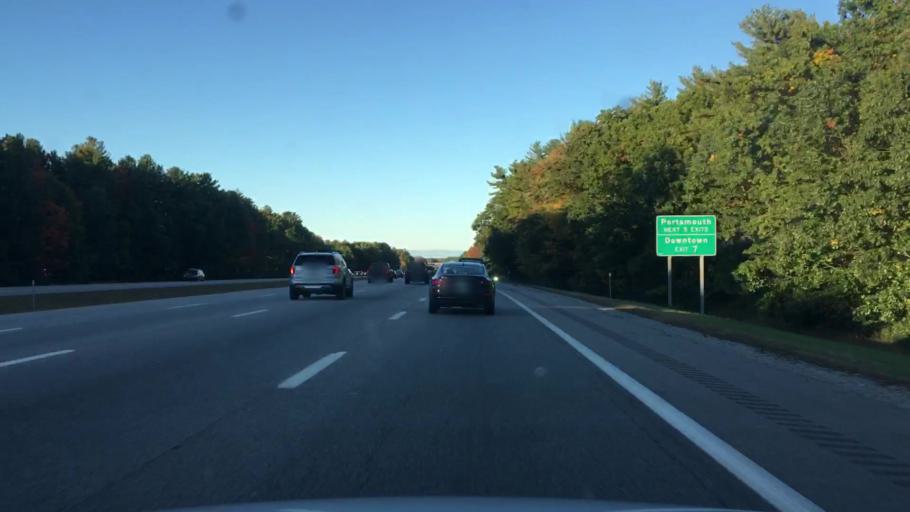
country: US
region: New Hampshire
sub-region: Rockingham County
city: Greenland
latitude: 43.0256
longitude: -70.8265
